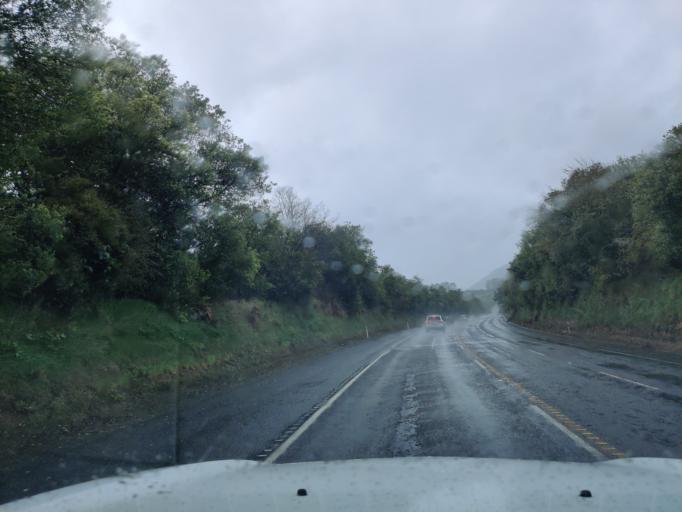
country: NZ
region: Bay of Plenty
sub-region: Rotorua District
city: Rotorua
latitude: -38.0729
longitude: 176.1755
